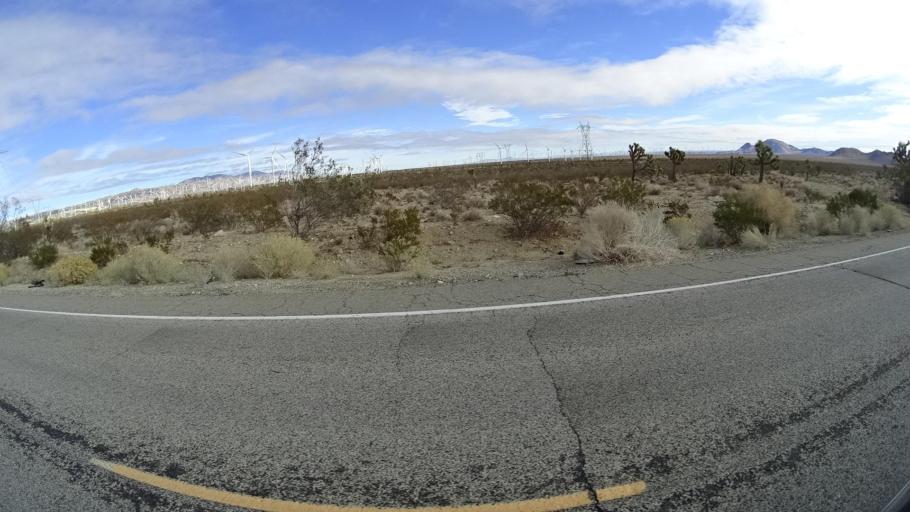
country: US
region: California
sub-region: Kern County
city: Mojave
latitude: 34.9882
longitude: -118.3216
